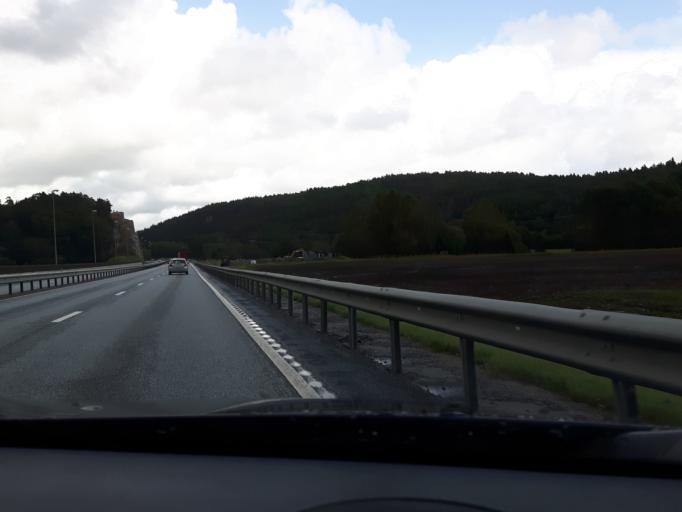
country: NO
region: Vest-Agder
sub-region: Sogne
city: Tangvall
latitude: 58.1044
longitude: 7.8249
